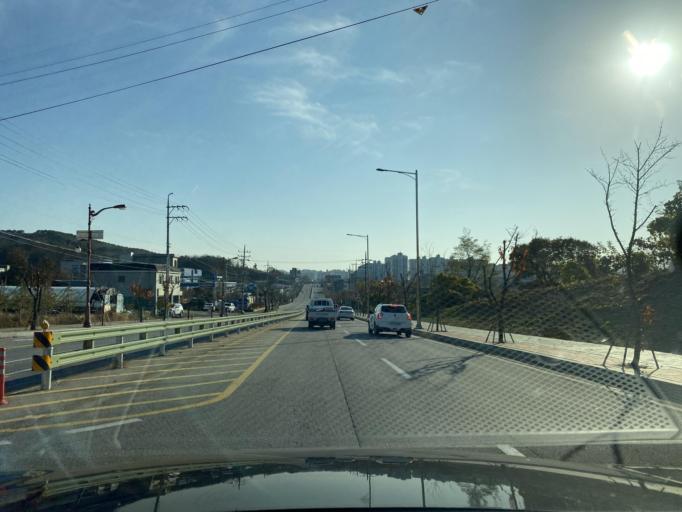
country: KR
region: Chungcheongnam-do
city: Yesan
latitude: 36.7038
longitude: 126.8388
